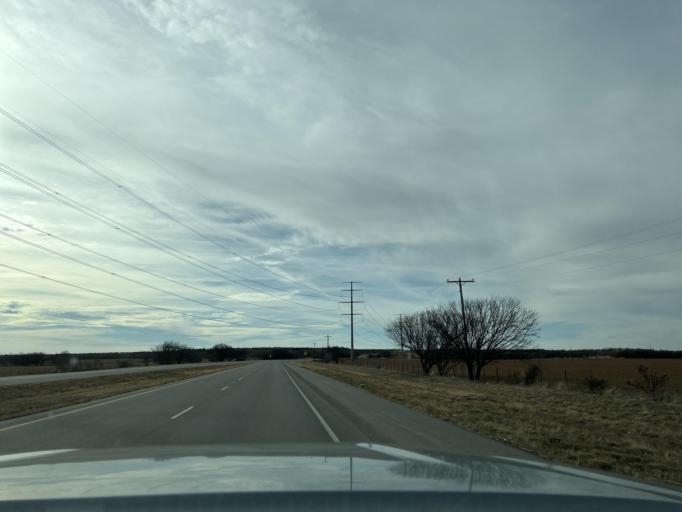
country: US
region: Texas
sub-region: Jones County
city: Stamford
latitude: 32.7513
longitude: -99.6277
